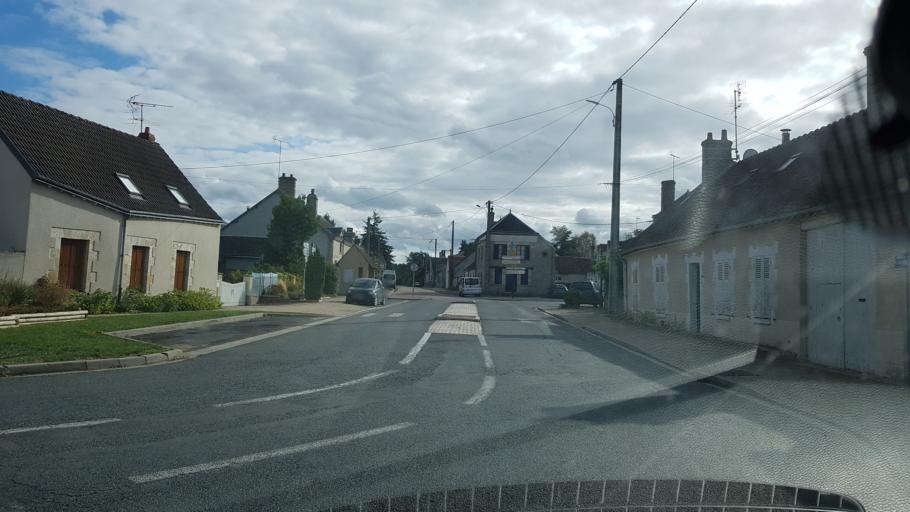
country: FR
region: Centre
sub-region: Departement du Loiret
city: Chilleurs-aux-Bois
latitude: 48.0637
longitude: 2.2139
